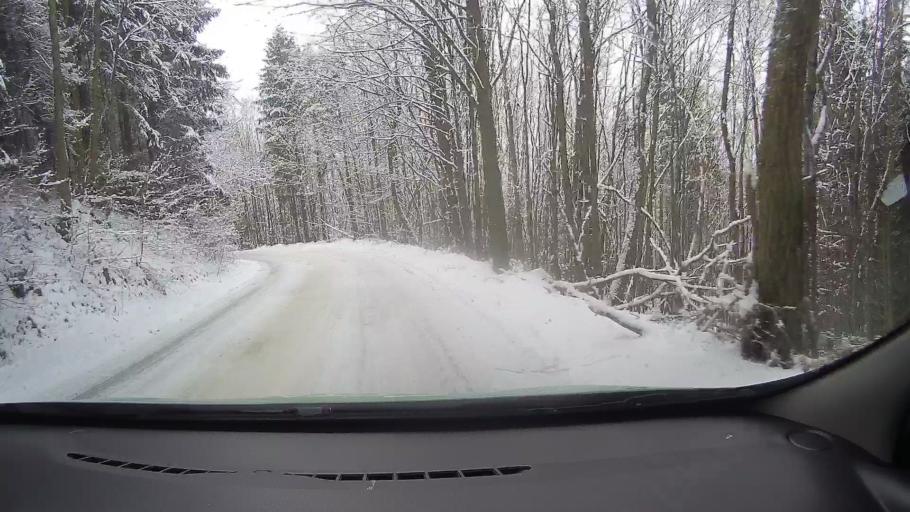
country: RO
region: Alba
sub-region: Comuna Almasu Mare
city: Almasu Mare
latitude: 46.0975
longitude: 23.1502
